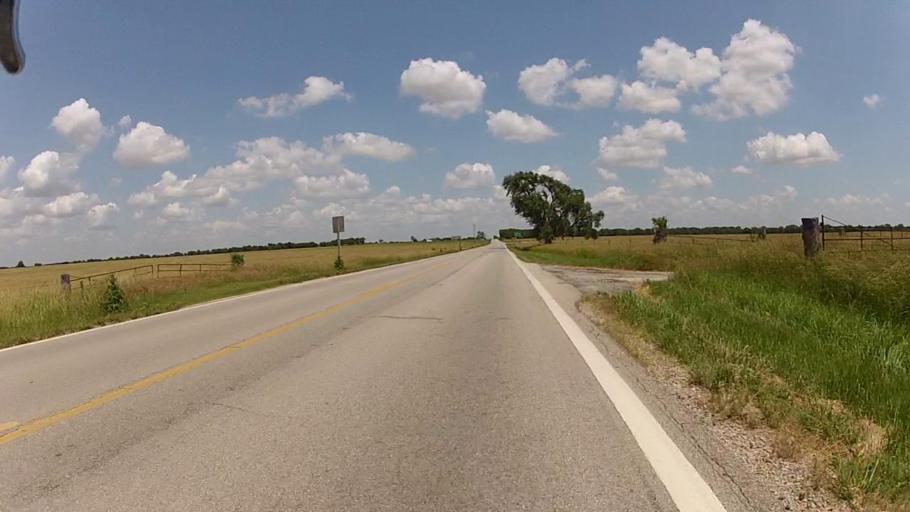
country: US
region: Kansas
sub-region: Labette County
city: Altamont
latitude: 37.1925
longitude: -95.3610
